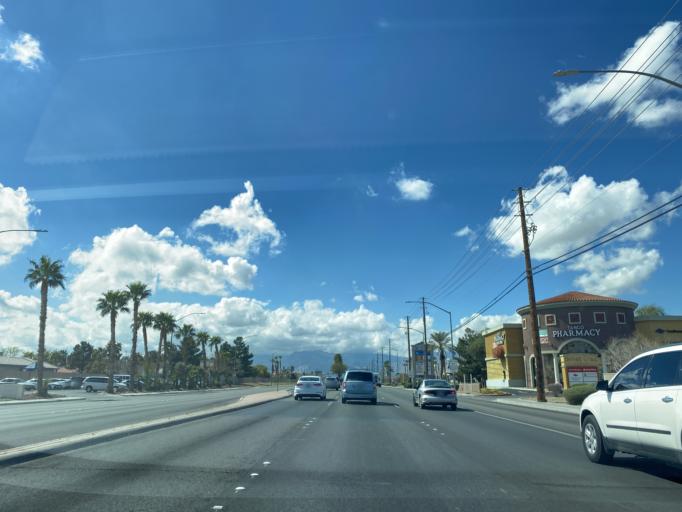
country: US
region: Nevada
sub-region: Clark County
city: Las Vegas
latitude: 36.2393
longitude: -115.1942
